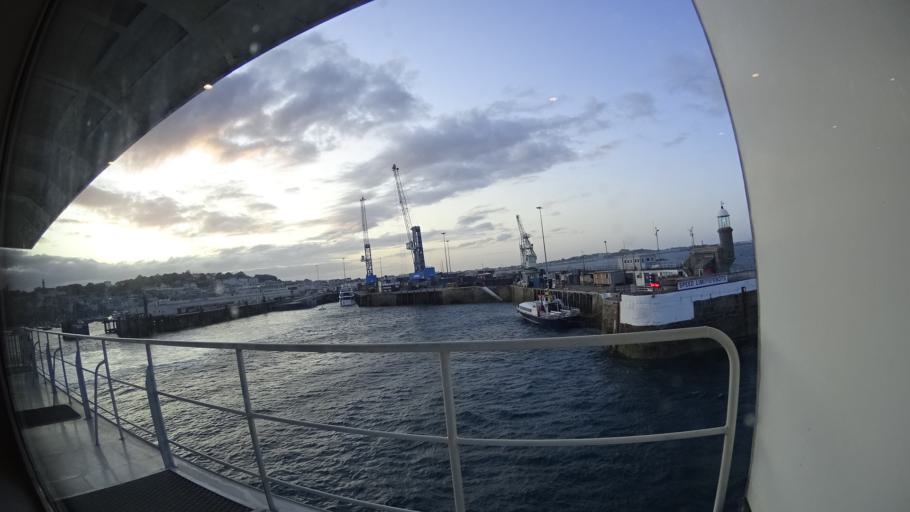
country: GG
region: St Peter Port
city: Saint Peter Port
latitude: 49.4562
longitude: -2.5268
